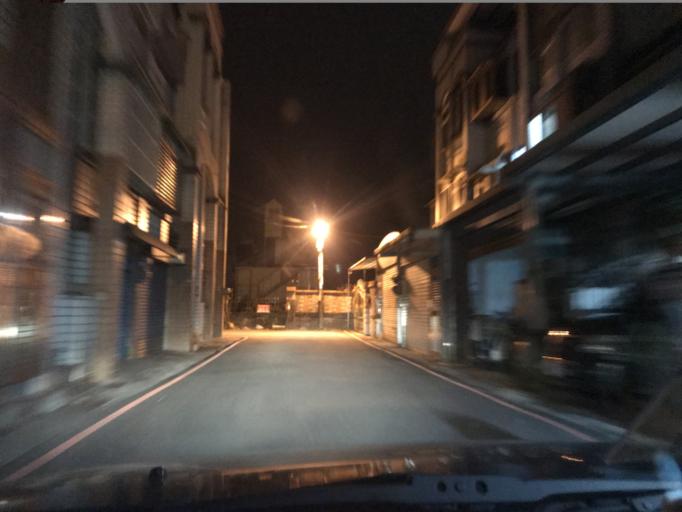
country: TW
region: Taiwan
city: Daxi
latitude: 24.8481
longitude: 121.2138
